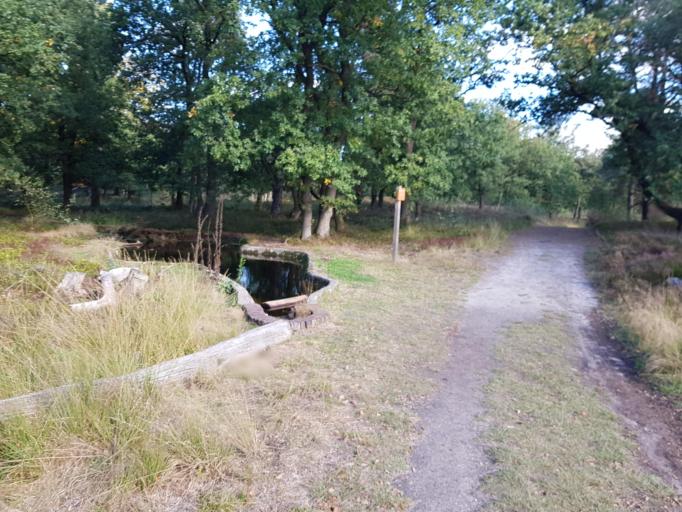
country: NL
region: Gelderland
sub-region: Gemeente Apeldoorn
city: Uddel
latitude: 52.3050
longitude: 5.8186
